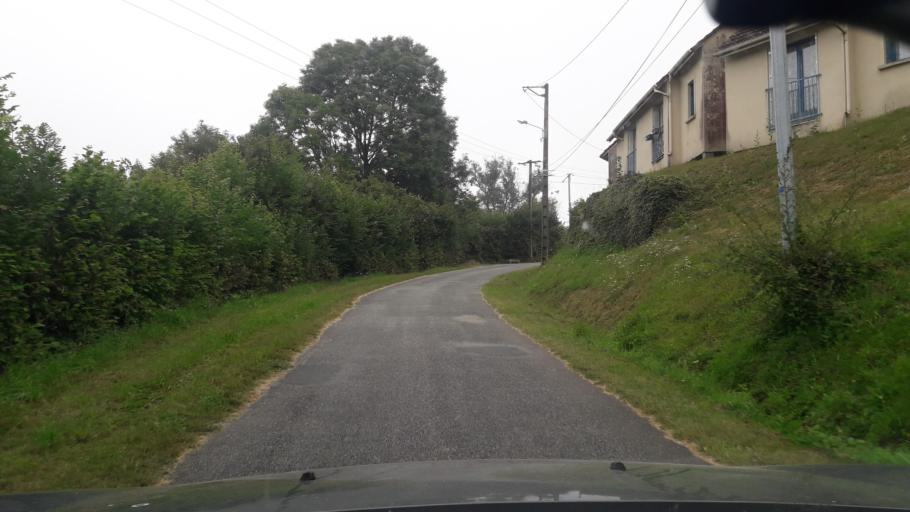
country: FR
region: Limousin
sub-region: Departement de la Creuse
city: Gouzon
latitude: 46.1115
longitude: 2.1685
